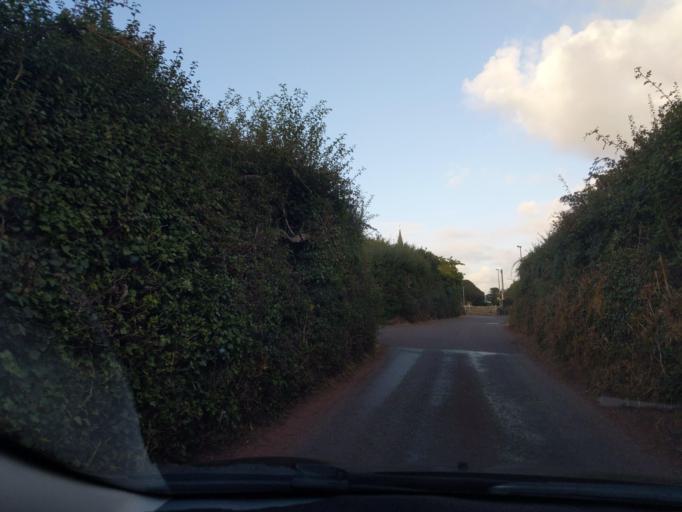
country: GB
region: England
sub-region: Devon
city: Salcombe
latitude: 50.2435
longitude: -3.8174
